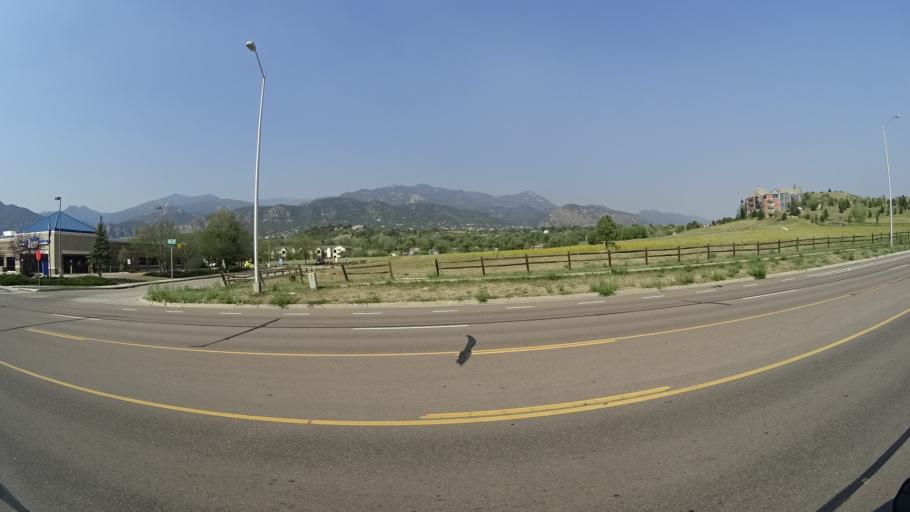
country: US
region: Colorado
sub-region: El Paso County
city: Colorado Springs
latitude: 38.8116
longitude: -104.8407
